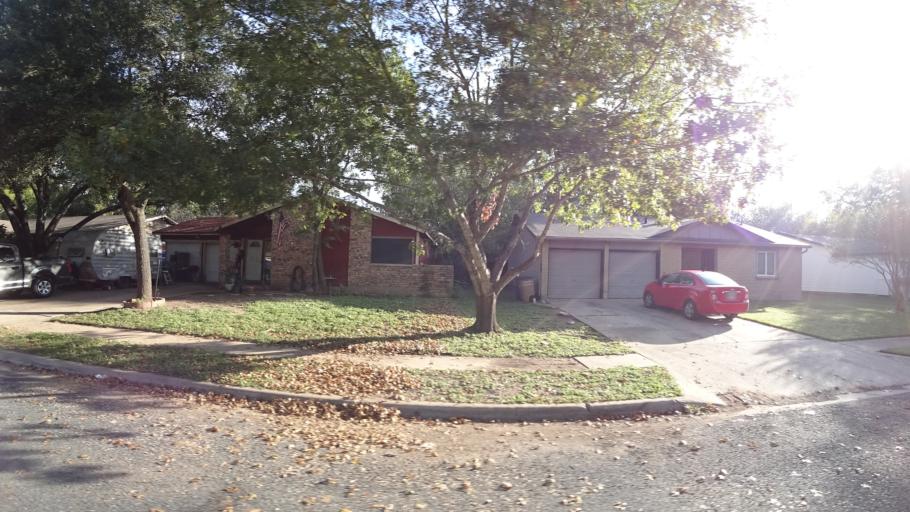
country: US
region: Texas
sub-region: Travis County
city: Onion Creek
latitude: 30.1912
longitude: -97.7505
